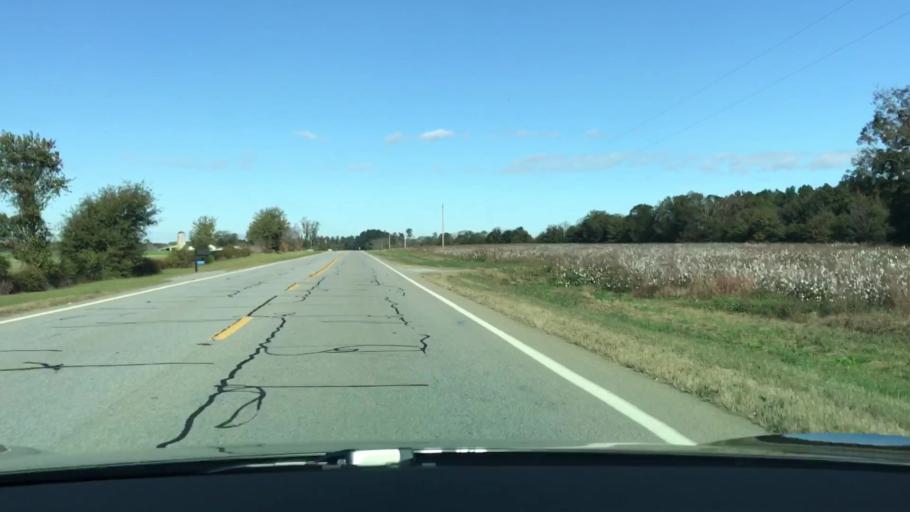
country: US
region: Georgia
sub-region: Warren County
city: Warrenton
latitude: 33.3647
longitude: -82.5985
